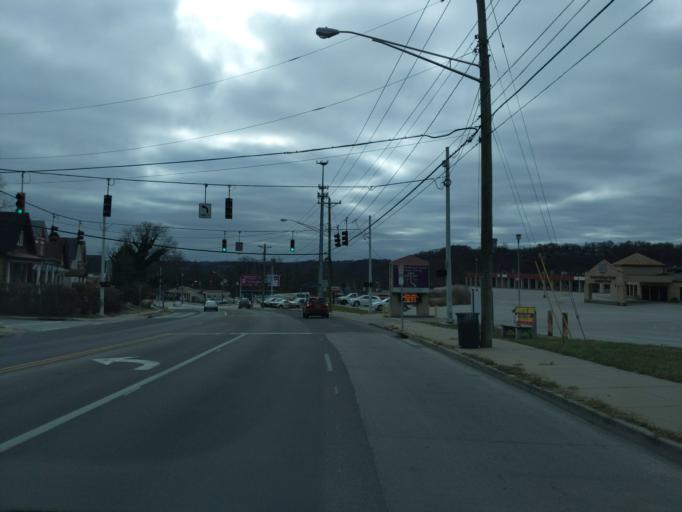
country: US
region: Ohio
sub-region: Hamilton County
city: Finneytown
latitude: 39.1800
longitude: -84.5447
